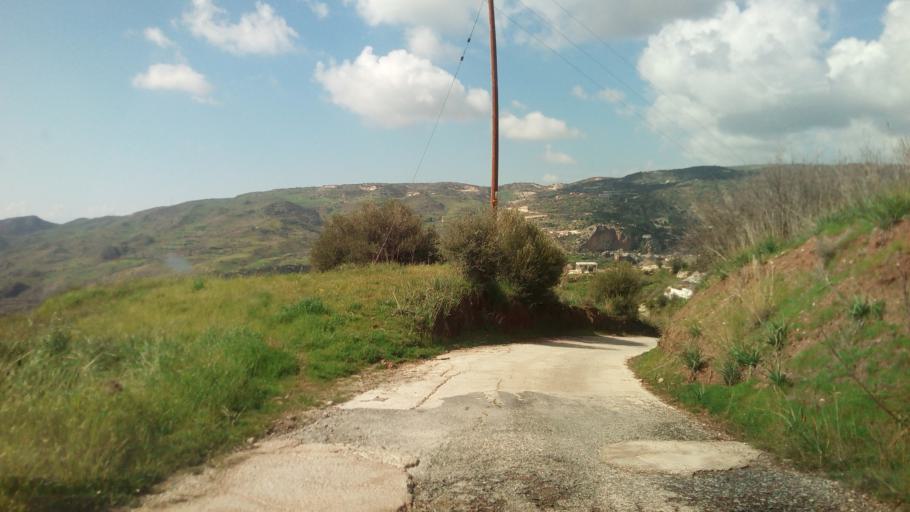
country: CY
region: Pafos
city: Mesogi
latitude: 34.7887
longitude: 32.5429
